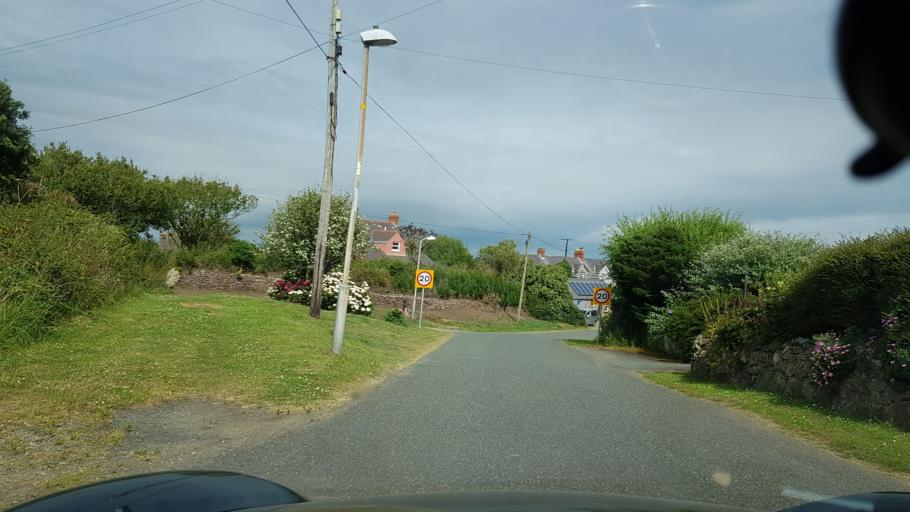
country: GB
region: Wales
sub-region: Pembrokeshire
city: Dale
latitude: 51.7328
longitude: -5.2015
